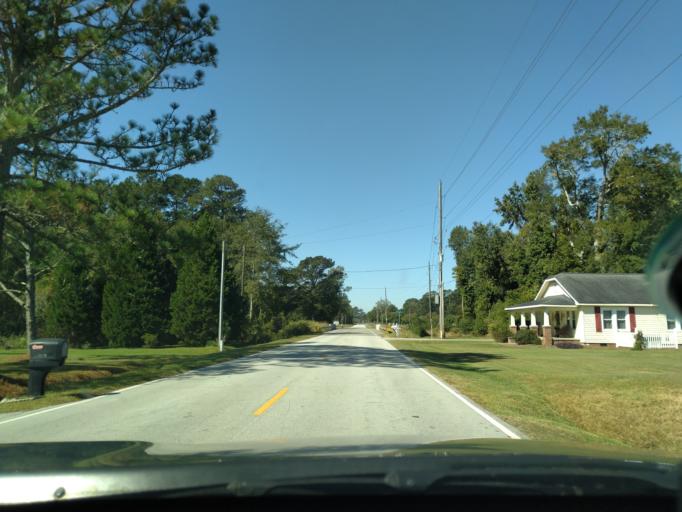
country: US
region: North Carolina
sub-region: Beaufort County
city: River Road
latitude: 35.5739
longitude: -76.9299
